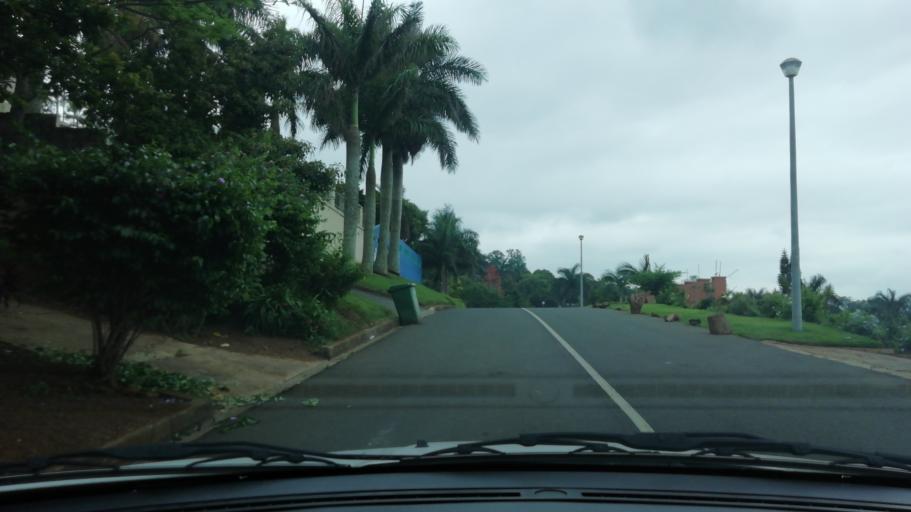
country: ZA
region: KwaZulu-Natal
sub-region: uThungulu District Municipality
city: Empangeni
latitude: -28.7623
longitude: 31.8876
